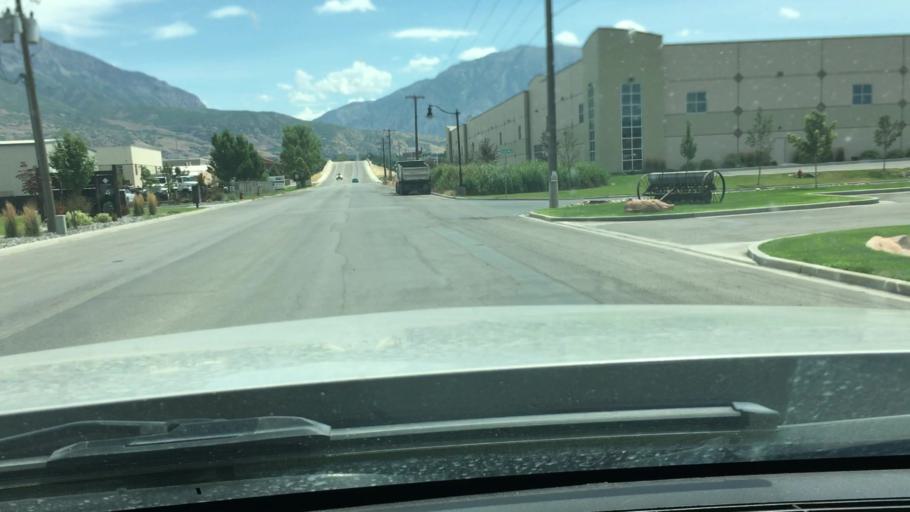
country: US
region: Utah
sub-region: Utah County
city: Lindon
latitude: 40.3335
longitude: -111.7495
